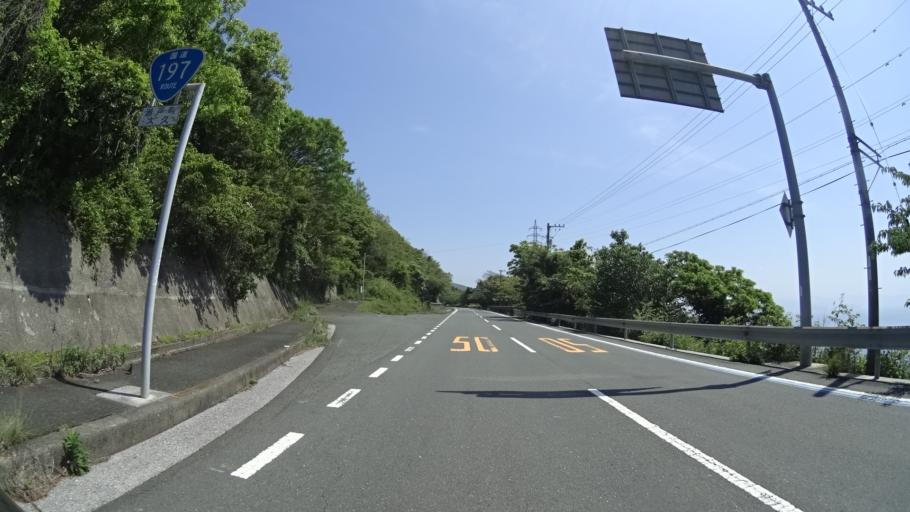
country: JP
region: Ehime
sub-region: Nishiuwa-gun
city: Ikata-cho
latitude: 33.4213
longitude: 132.2038
